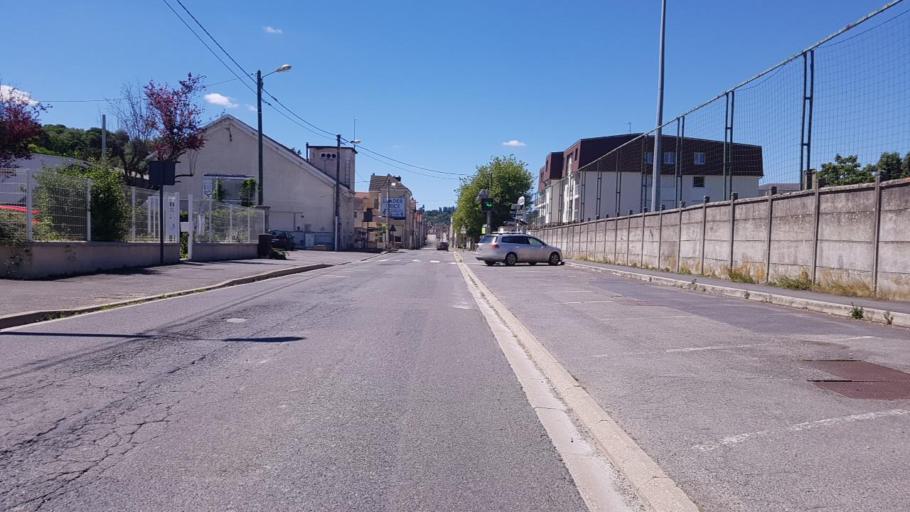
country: FR
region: Ile-de-France
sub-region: Departement de Seine-et-Marne
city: La Ferte-sous-Jouarre
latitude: 48.9512
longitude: 3.1373
